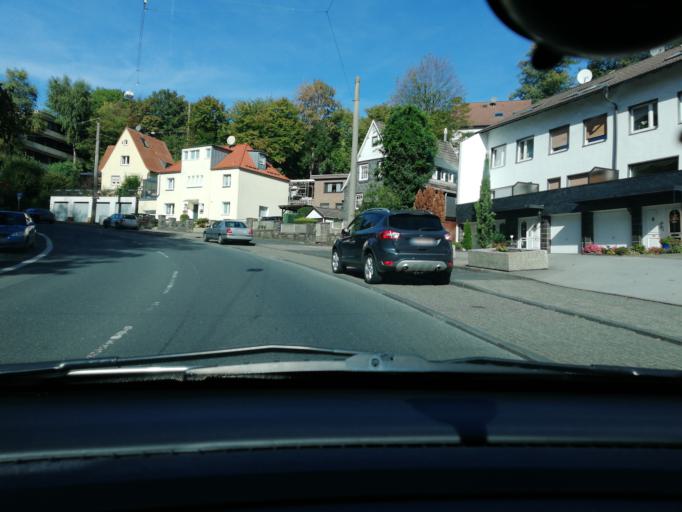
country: DE
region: North Rhine-Westphalia
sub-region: Regierungsbezirk Dusseldorf
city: Wuppertal
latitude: 51.2864
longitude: 7.2056
